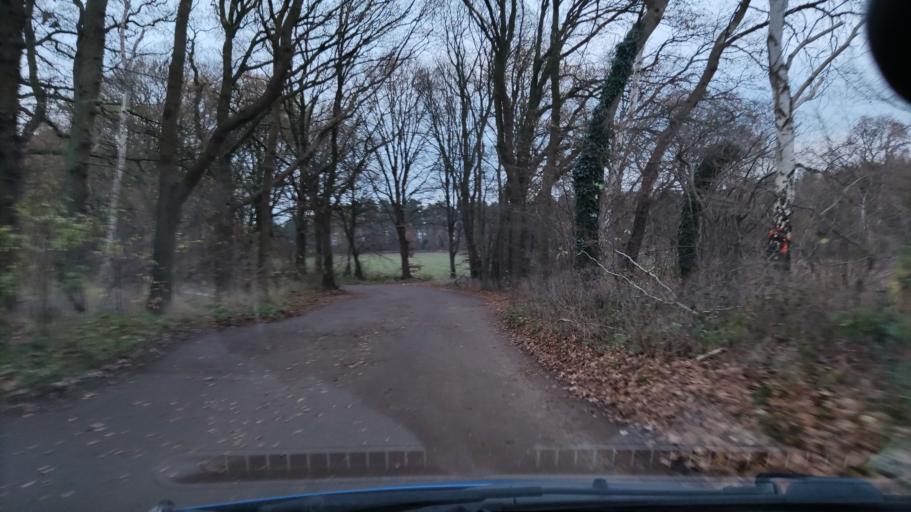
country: DE
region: Lower Saxony
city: Vogelsen
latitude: 53.2687
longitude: 10.3530
